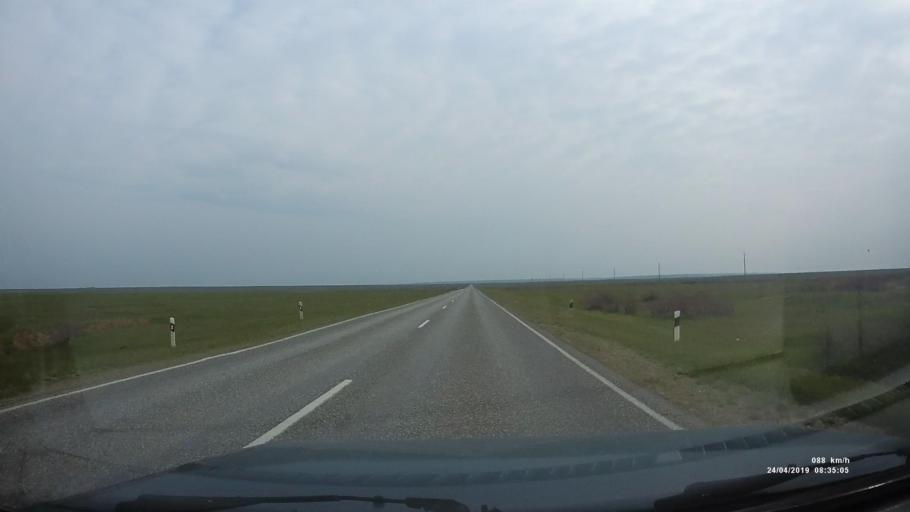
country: RU
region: Kalmykiya
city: Arshan'
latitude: 46.1949
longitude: 43.9138
